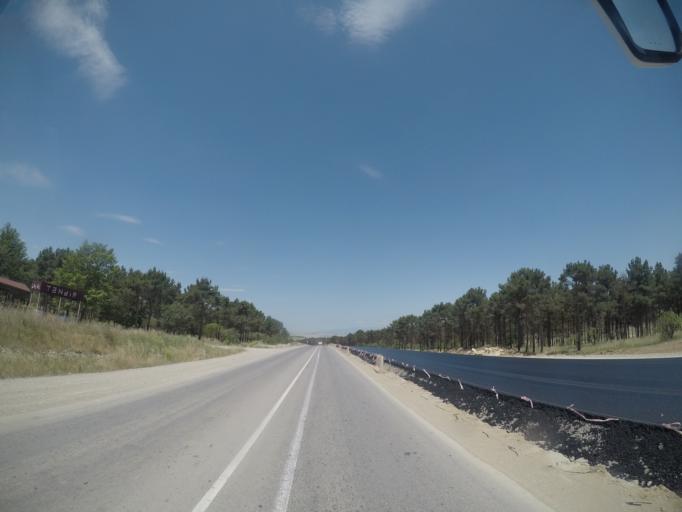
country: AZ
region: Qobustan
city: Qobustan
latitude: 40.5261
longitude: 48.8009
